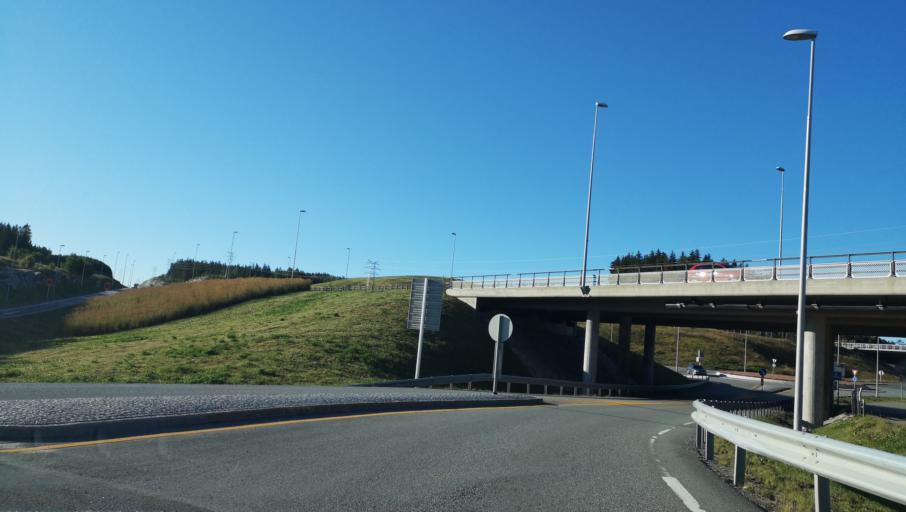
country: NO
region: Ostfold
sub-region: Hobol
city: Knappstad
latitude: 59.6193
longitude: 11.0056
